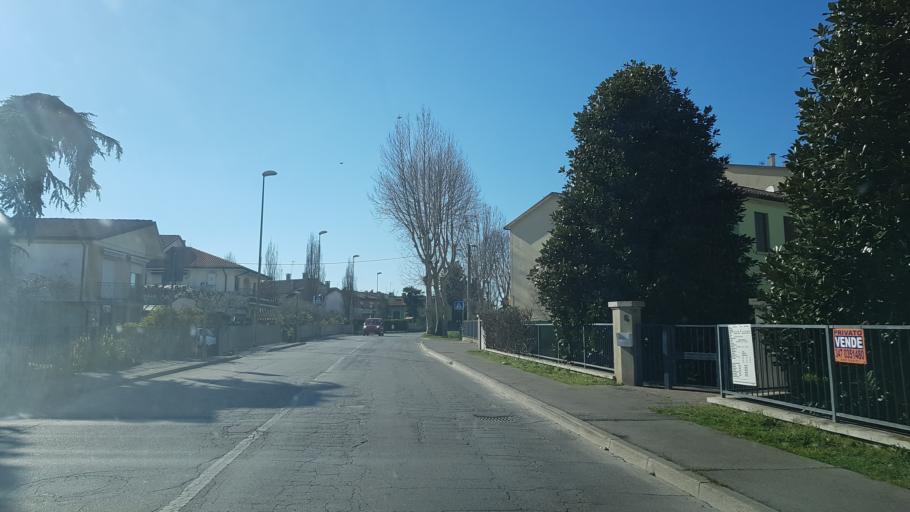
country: IT
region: Veneto
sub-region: Provincia di Rovigo
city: Adria
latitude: 45.0583
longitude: 12.0524
